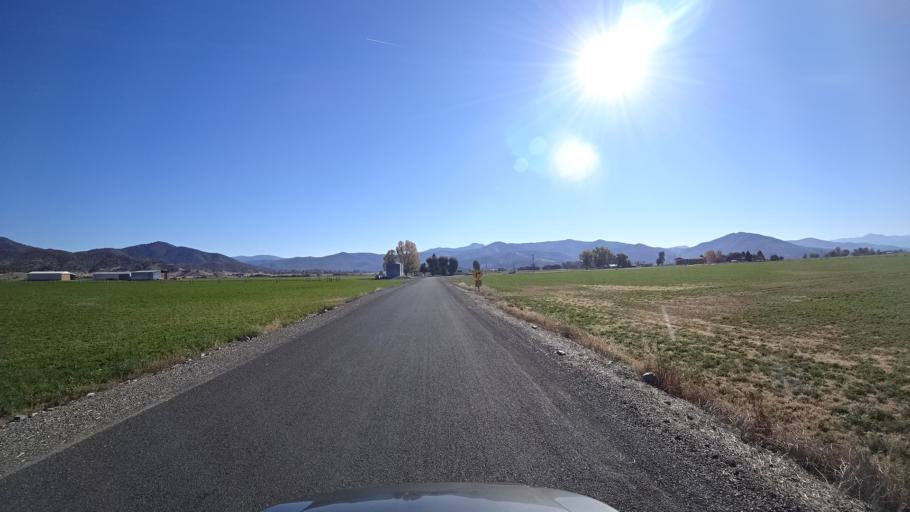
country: US
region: California
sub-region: Siskiyou County
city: Yreka
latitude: 41.5754
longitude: -122.8575
